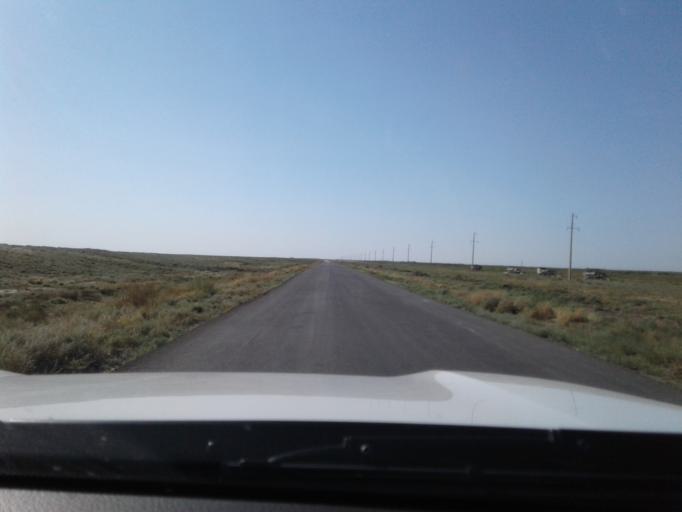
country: IR
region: Razavi Khorasan
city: Kalat-e Naderi
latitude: 37.1425
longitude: 60.0686
